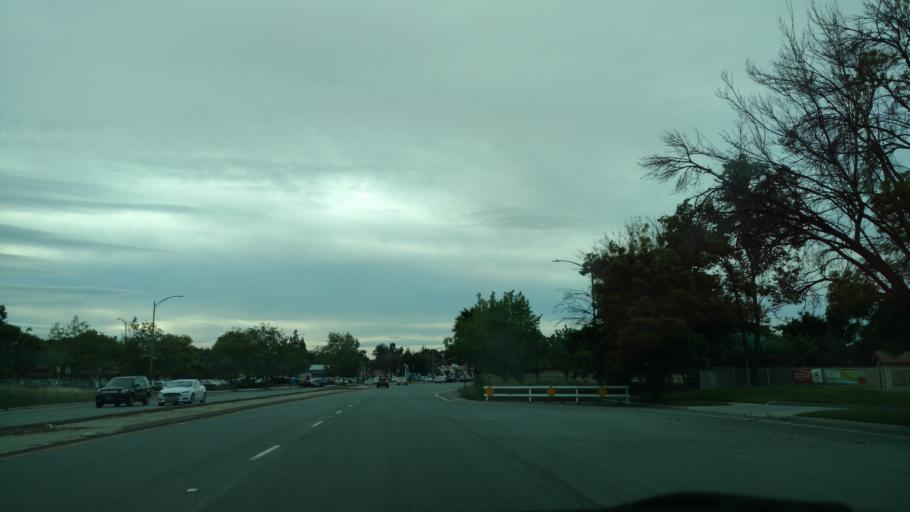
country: US
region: California
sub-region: Santa Clara County
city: Seven Trees
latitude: 37.3128
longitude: -121.7895
